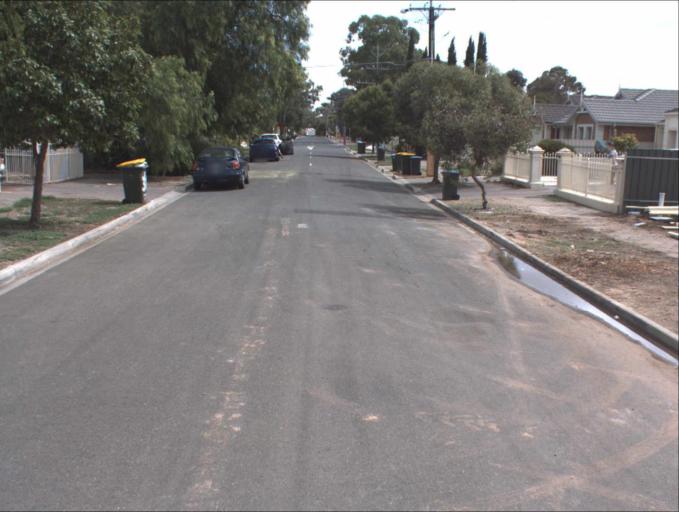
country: AU
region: South Australia
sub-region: Campbelltown
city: Paradise
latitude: -34.8634
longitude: 138.6578
